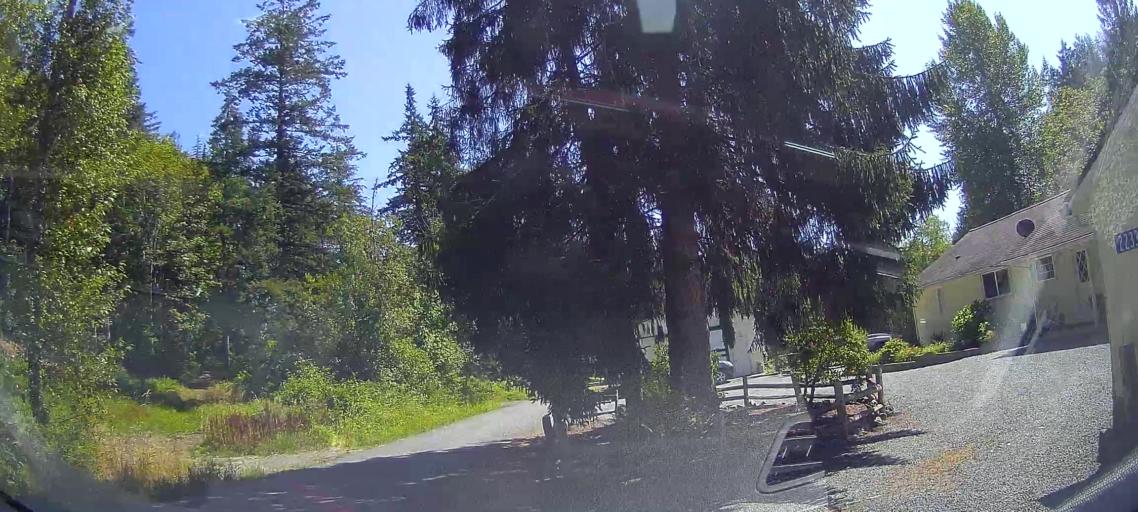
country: US
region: Washington
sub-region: Skagit County
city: Big Lake
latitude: 48.4318
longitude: -122.2624
